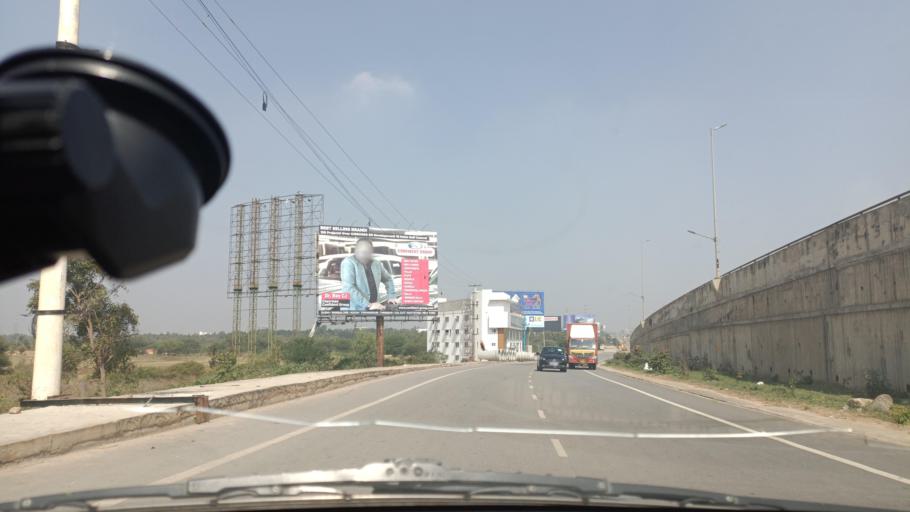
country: IN
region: Karnataka
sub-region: Bangalore Urban
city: Yelahanka
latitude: 13.1741
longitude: 77.6338
